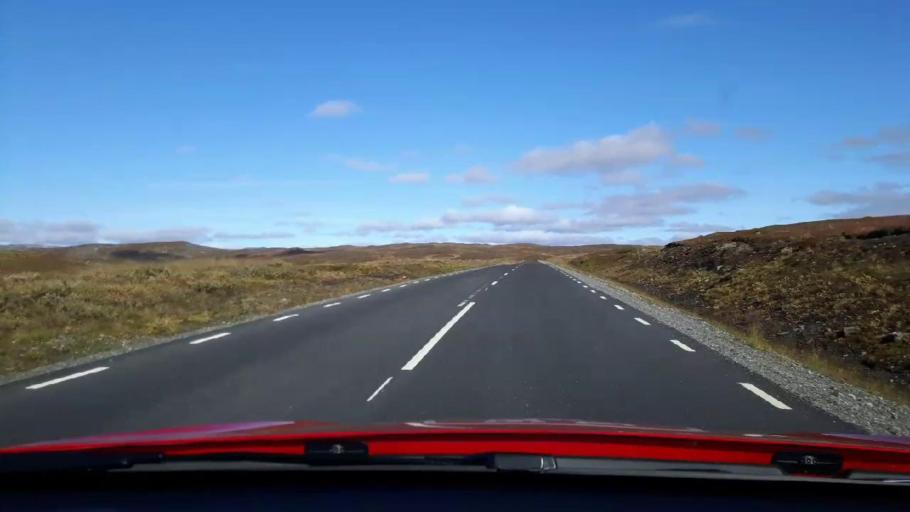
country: NO
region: Nordland
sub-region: Hattfjelldal
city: Hattfjelldal
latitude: 65.0399
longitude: 14.3274
